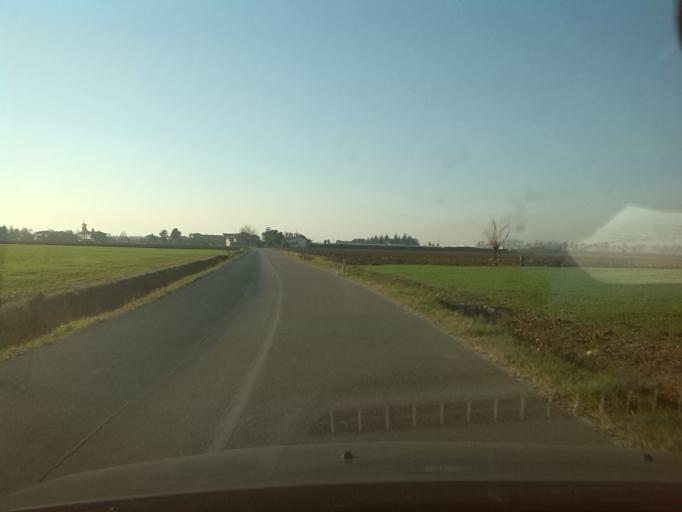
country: IT
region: Friuli Venezia Giulia
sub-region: Provincia di Udine
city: Trivignano Udinese
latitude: 45.9563
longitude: 13.3298
